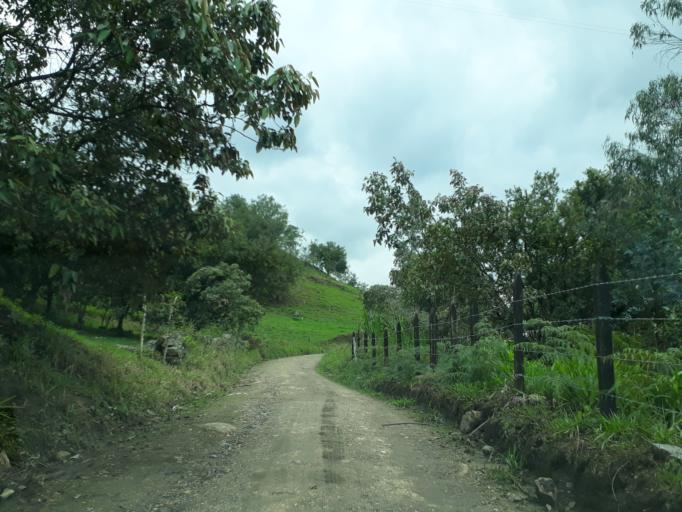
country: CO
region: Cundinamarca
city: Manta
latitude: 4.9849
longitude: -73.5576
